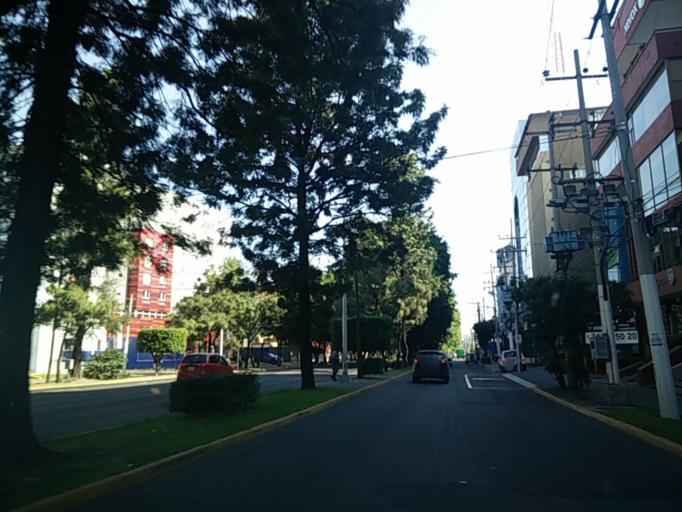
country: MX
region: Jalisco
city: Guadalajara
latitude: 20.6509
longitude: -103.3984
